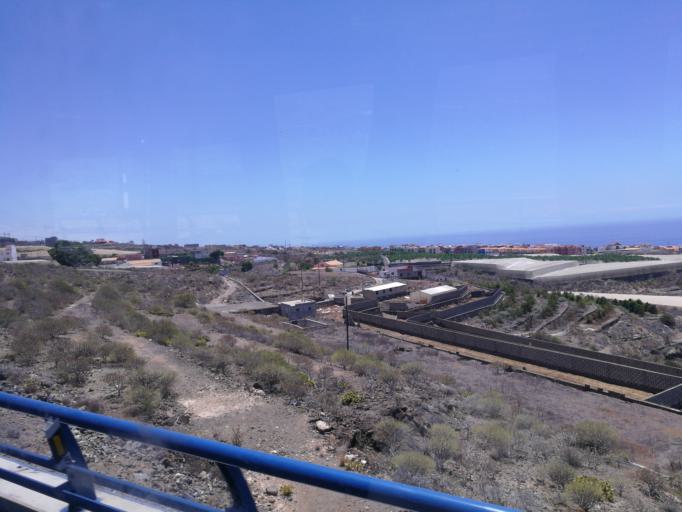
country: ES
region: Canary Islands
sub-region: Provincia de Santa Cruz de Tenerife
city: Guia de Isora
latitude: 28.1859
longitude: -16.7887
